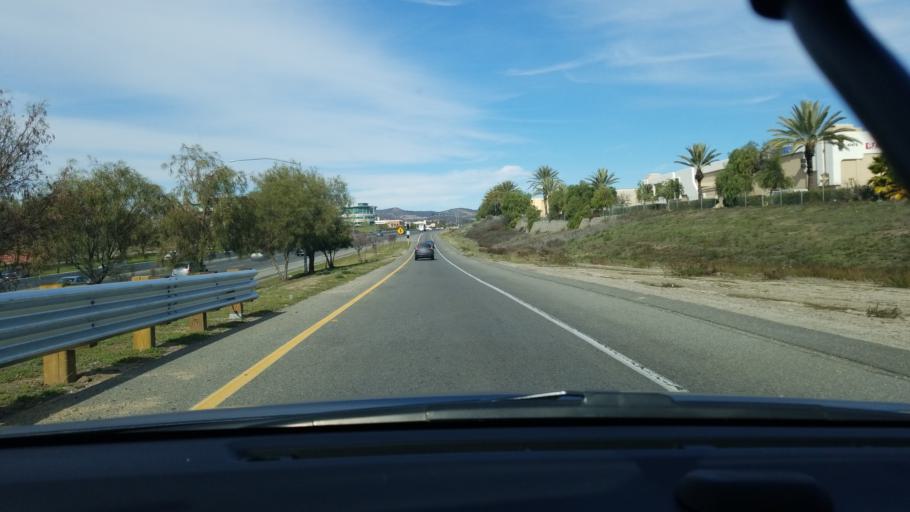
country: US
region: California
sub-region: Riverside County
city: Murrieta Hot Springs
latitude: 33.5575
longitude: -117.1804
